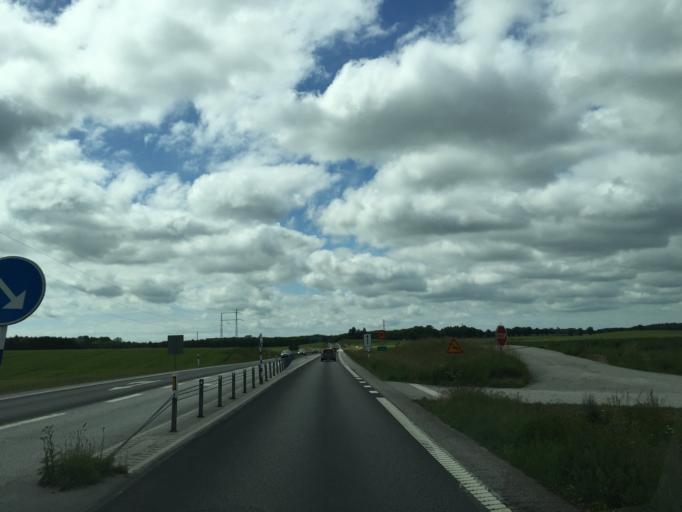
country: SE
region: Skane
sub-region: Trelleborgs Kommun
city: Anderslov
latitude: 55.5048
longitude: 13.3507
